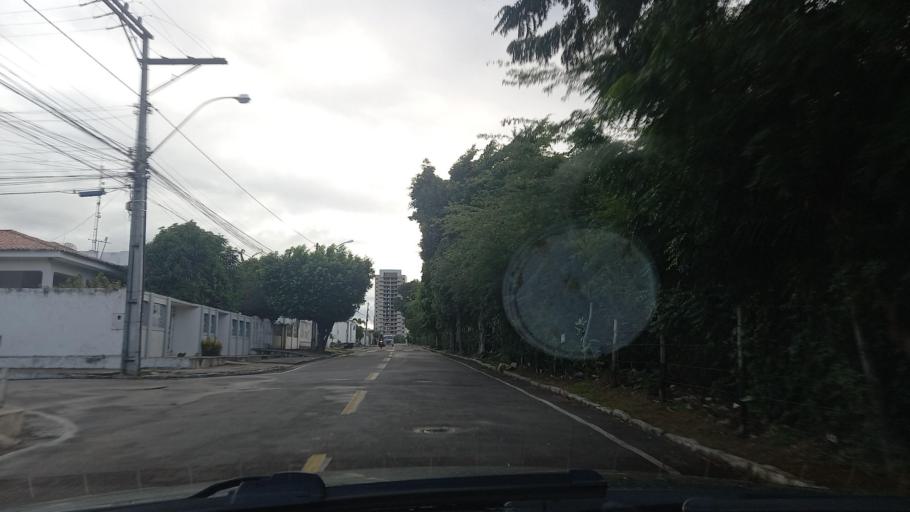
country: BR
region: Bahia
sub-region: Paulo Afonso
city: Paulo Afonso
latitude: -9.3977
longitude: -38.2280
